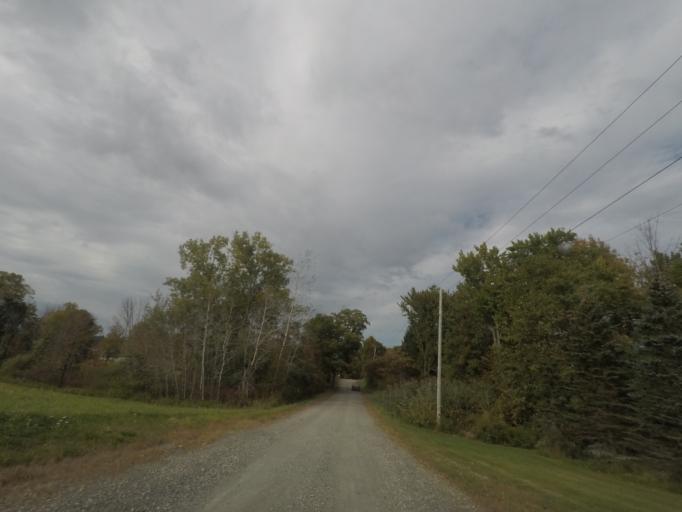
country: US
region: New York
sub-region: Rensselaer County
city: West Sand Lake
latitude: 42.5850
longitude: -73.6129
